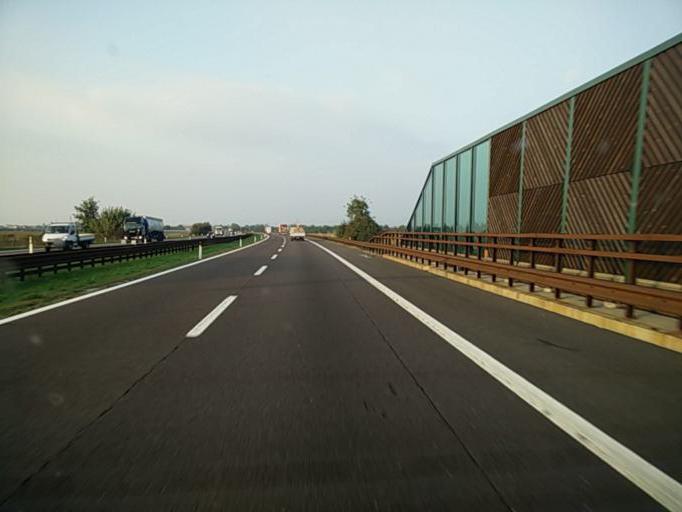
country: IT
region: Veneto
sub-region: Provincia di Verona
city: Alpo
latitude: 45.3572
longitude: 10.9205
